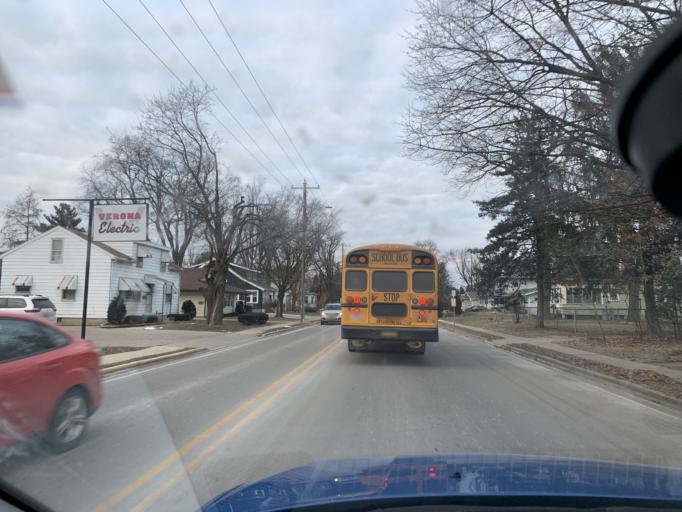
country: US
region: Wisconsin
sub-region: Dane County
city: Verona
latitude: 42.9920
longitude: -89.5335
